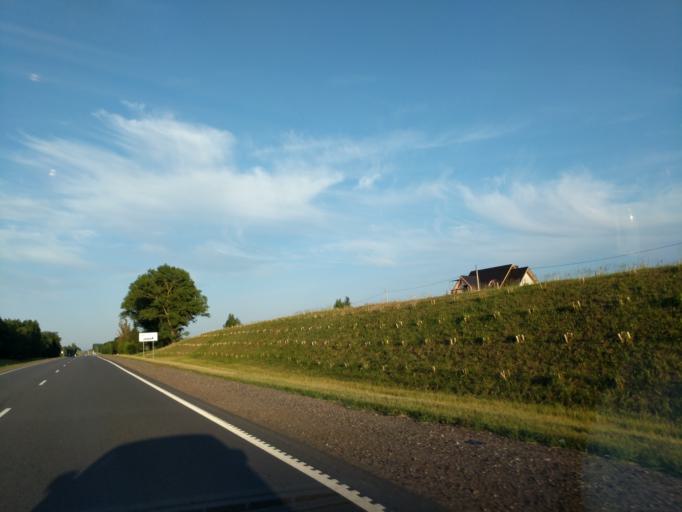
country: BY
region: Minsk
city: Syomkava
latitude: 54.0979
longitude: 27.4948
